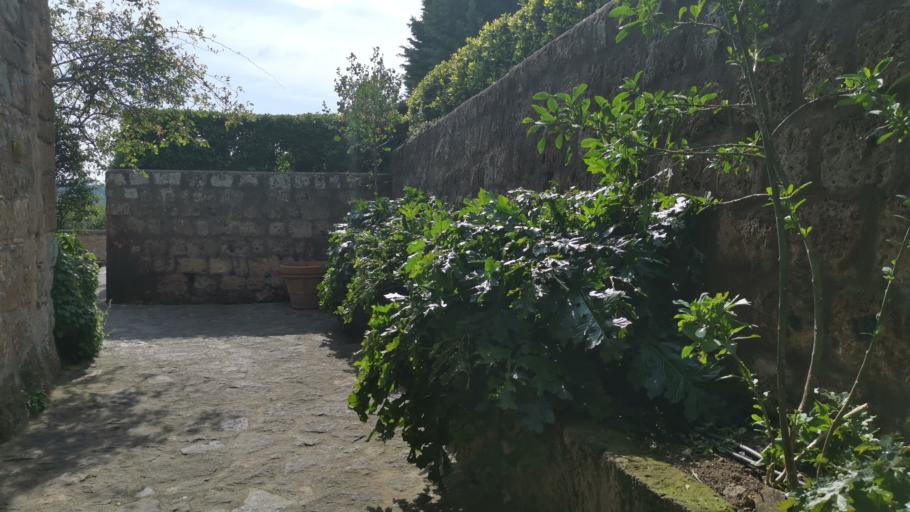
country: IT
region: Latium
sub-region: Provincia di Viterbo
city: Lubriano
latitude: 42.6274
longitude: 12.1140
